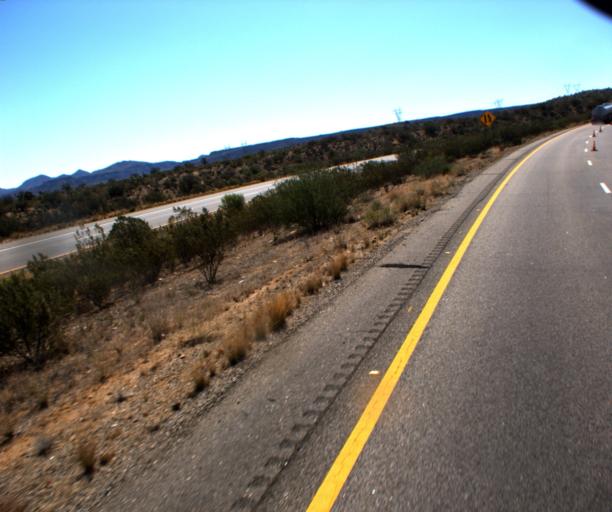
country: US
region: Arizona
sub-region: Yavapai County
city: Bagdad
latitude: 34.3671
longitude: -113.1787
